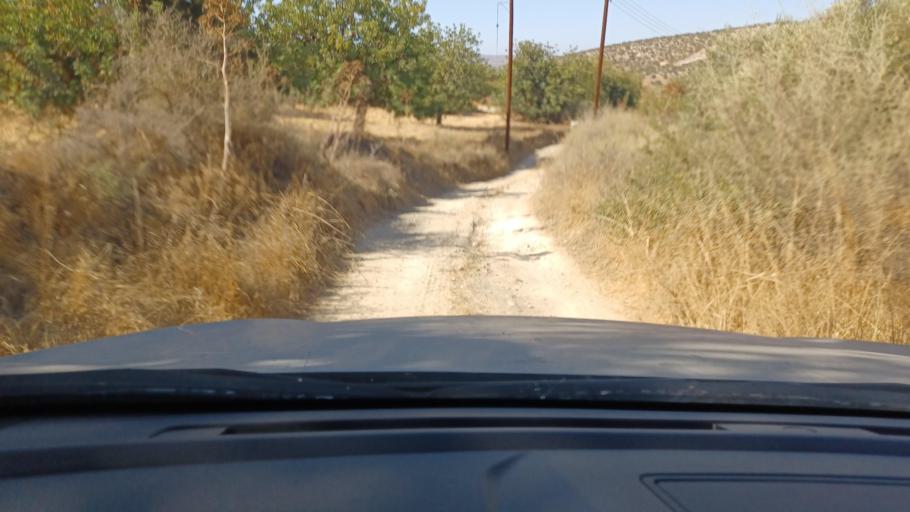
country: CY
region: Pafos
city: Polis
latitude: 35.0002
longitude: 32.5006
